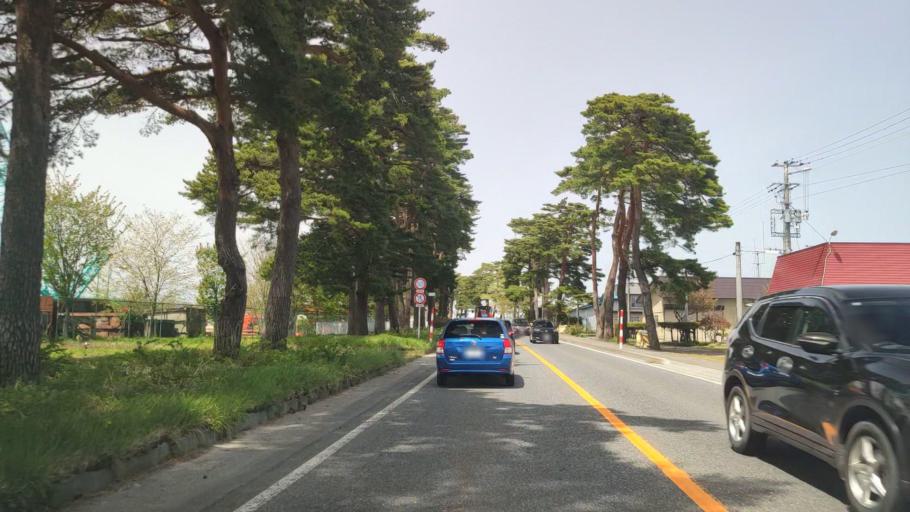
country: JP
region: Aomori
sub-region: Misawa Shi
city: Inuotose
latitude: 40.6703
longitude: 141.1838
